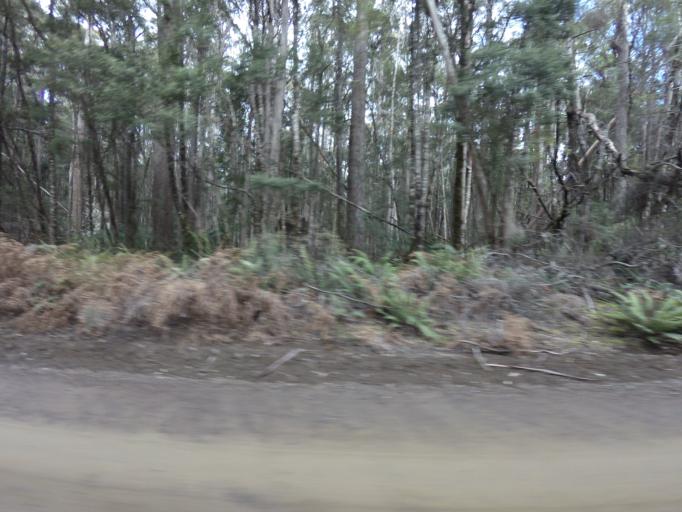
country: AU
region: Tasmania
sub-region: Huon Valley
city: Geeveston
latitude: -43.4024
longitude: 146.8642
